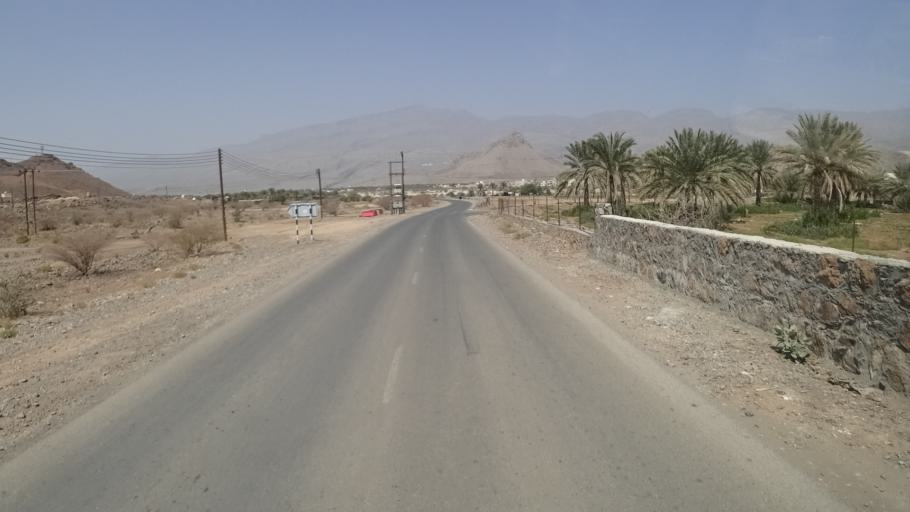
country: OM
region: Muhafazat ad Dakhiliyah
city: Bahla'
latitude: 23.0826
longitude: 57.3129
